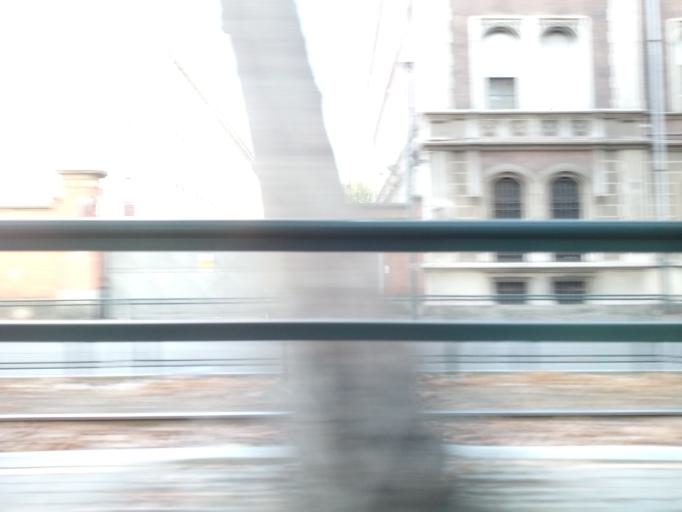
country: IT
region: Piedmont
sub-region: Provincia di Torino
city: Turin
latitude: 45.0438
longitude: 7.6587
